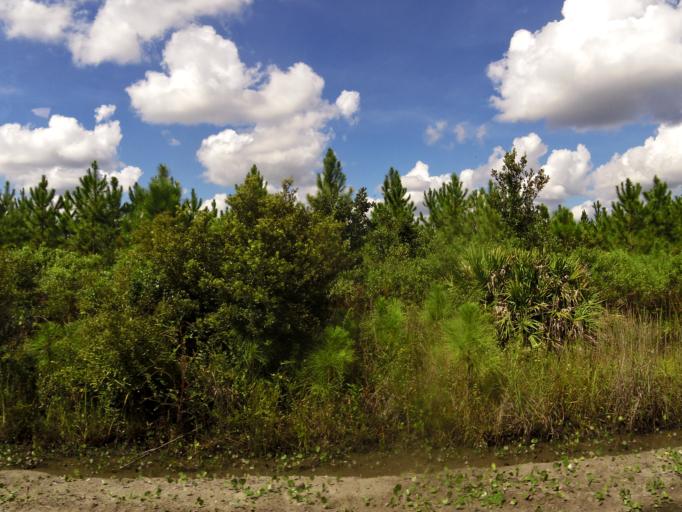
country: US
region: Georgia
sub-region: Clinch County
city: Homerville
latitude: 30.7417
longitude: -82.5941
